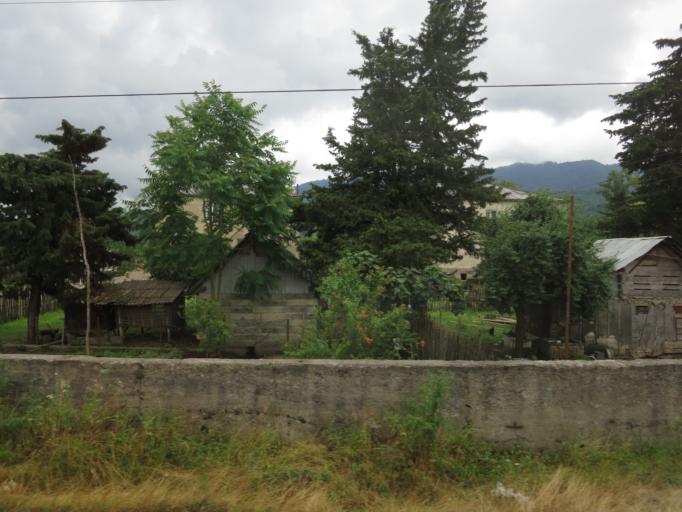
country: GE
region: Samegrelo and Zemo Svaneti
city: Abasha
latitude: 42.0963
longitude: 42.2356
